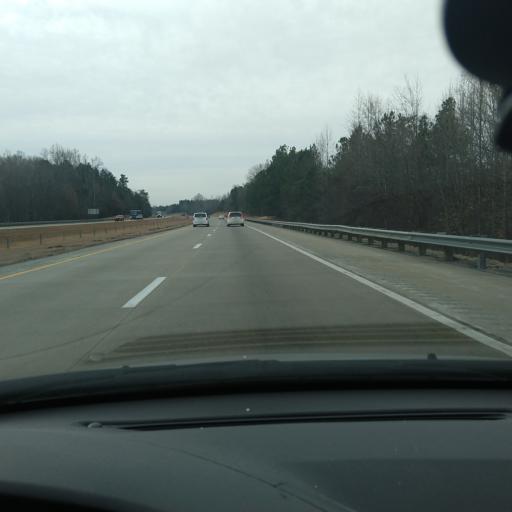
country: US
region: North Carolina
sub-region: Davidson County
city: Welcome
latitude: 35.9115
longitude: -80.2346
